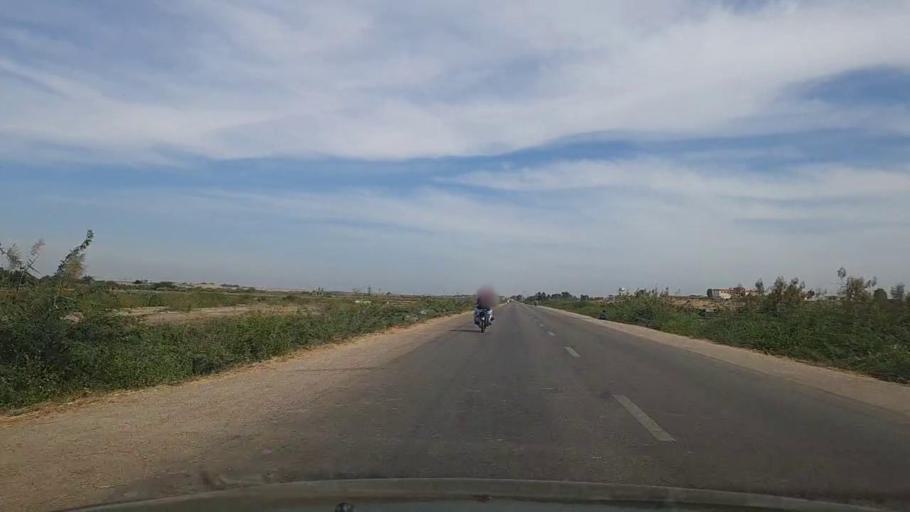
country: PK
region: Sindh
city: Thatta
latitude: 24.8146
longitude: 67.9795
